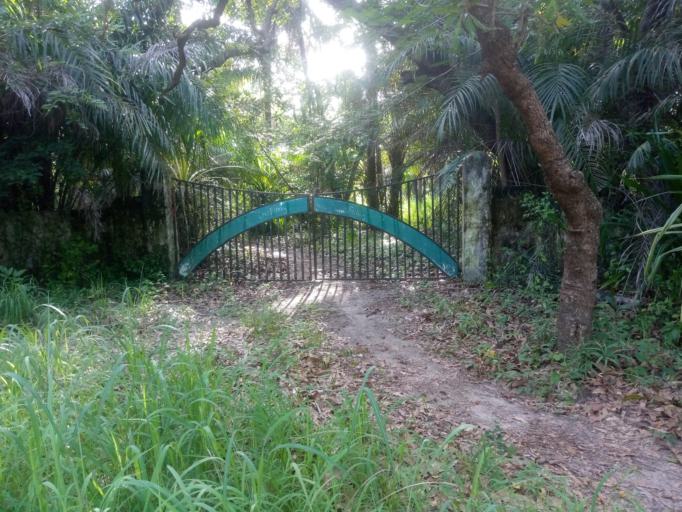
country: GM
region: Western
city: Gunjur
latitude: 13.0397
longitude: -16.7290
